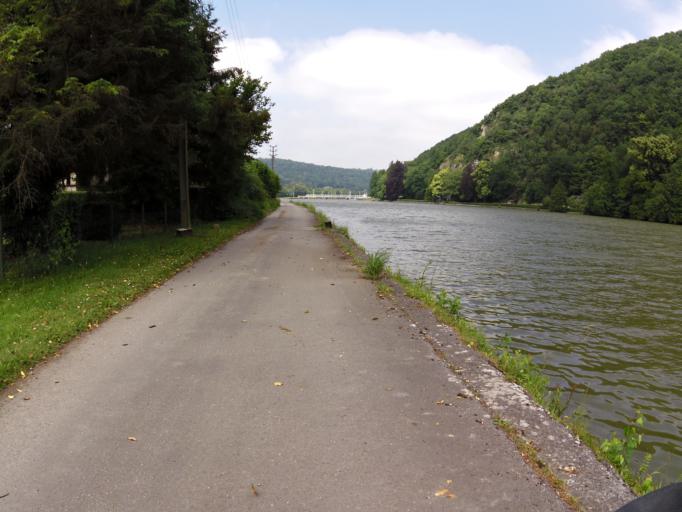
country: BE
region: Wallonia
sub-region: Province de Namur
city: Hastiere-Lavaux
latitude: 50.1946
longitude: 4.8229
